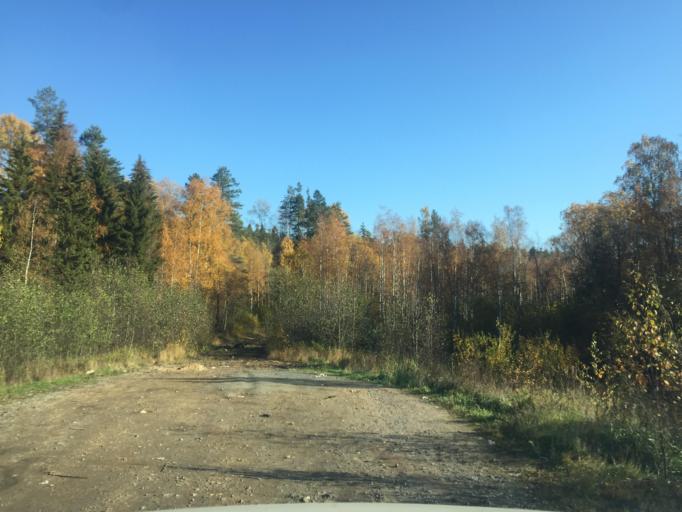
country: RU
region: Leningrad
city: Kuznechnoye
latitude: 61.1946
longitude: 29.8016
